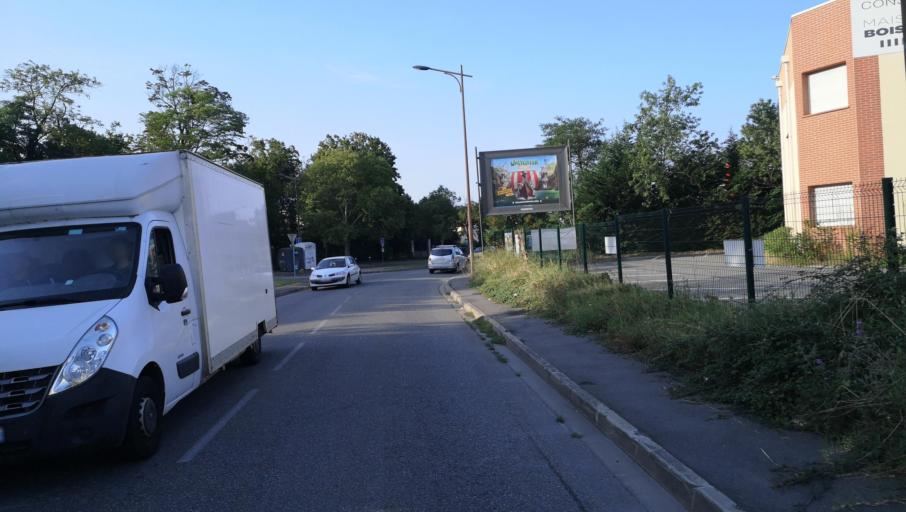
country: FR
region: Midi-Pyrenees
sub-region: Departement de la Haute-Garonne
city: Blagnac
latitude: 43.6043
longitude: 1.3943
